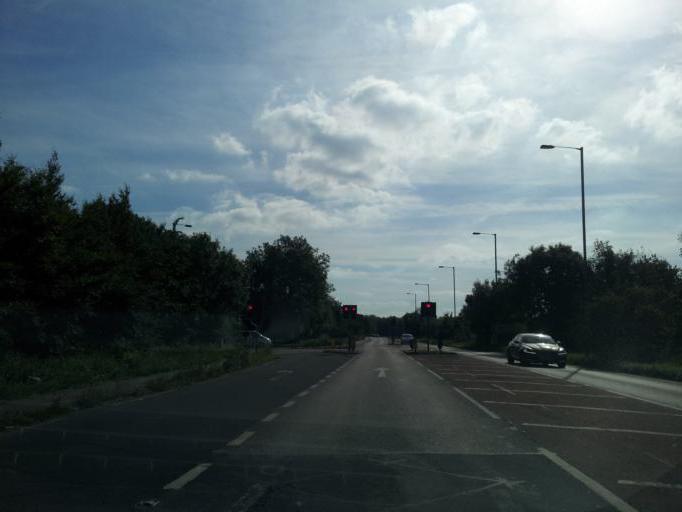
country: GB
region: England
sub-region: Cambridgeshire
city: Waterbeach
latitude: 52.2718
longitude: 0.1777
